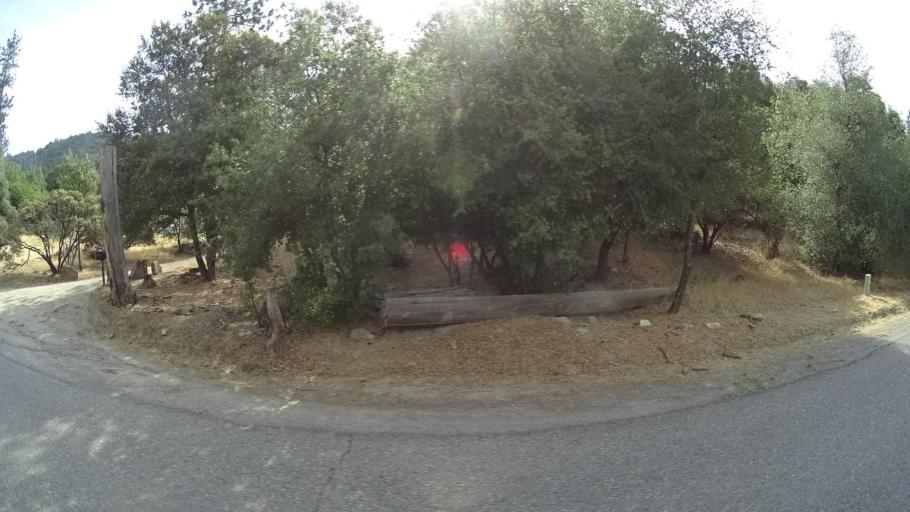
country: US
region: California
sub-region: Madera County
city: Ahwahnee
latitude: 37.4745
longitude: -119.7724
